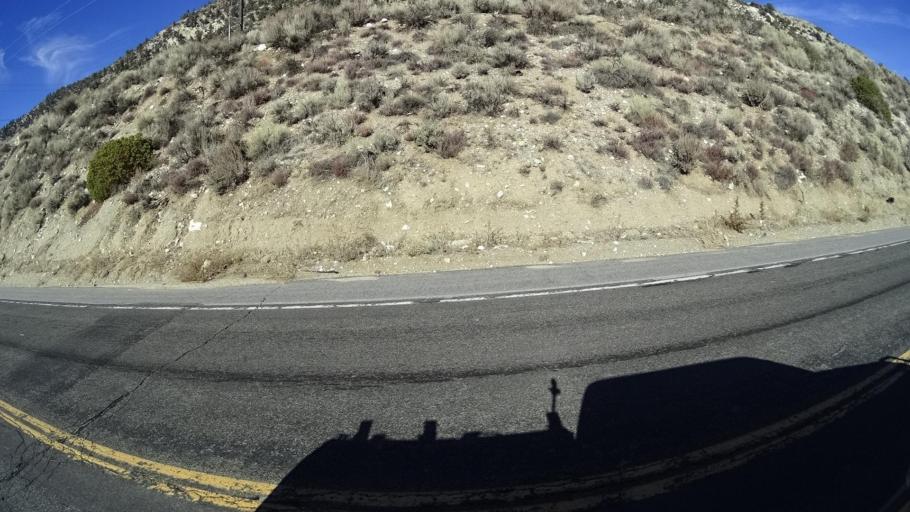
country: US
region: California
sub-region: Kern County
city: Frazier Park
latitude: 34.8197
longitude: -118.9828
